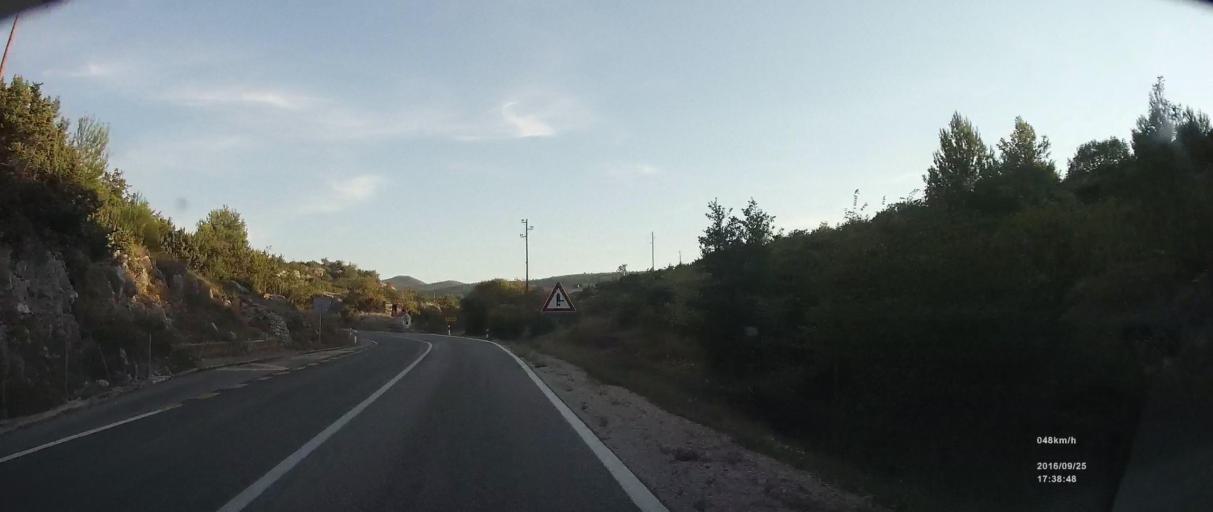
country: HR
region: Sibensko-Kniniska
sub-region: Grad Sibenik
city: Brodarica
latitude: 43.6486
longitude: 16.0574
